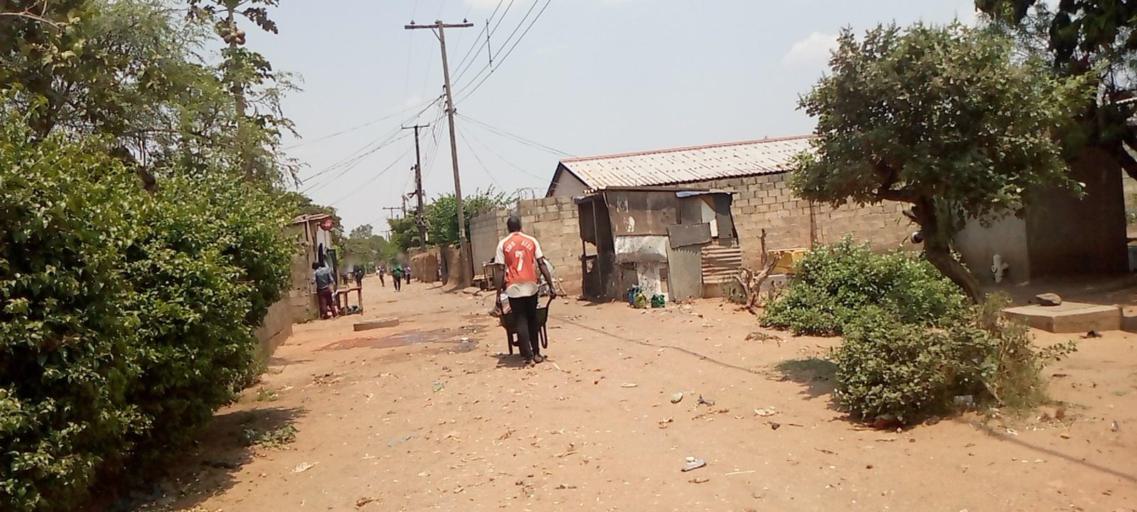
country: ZM
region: Lusaka
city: Lusaka
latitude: -15.3997
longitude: 28.3489
